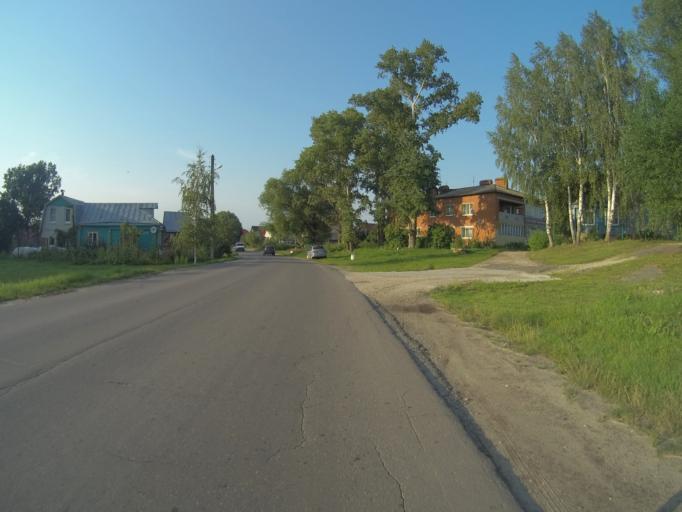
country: RU
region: Vladimir
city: Bogolyubovo
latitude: 56.2684
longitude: 40.4827
